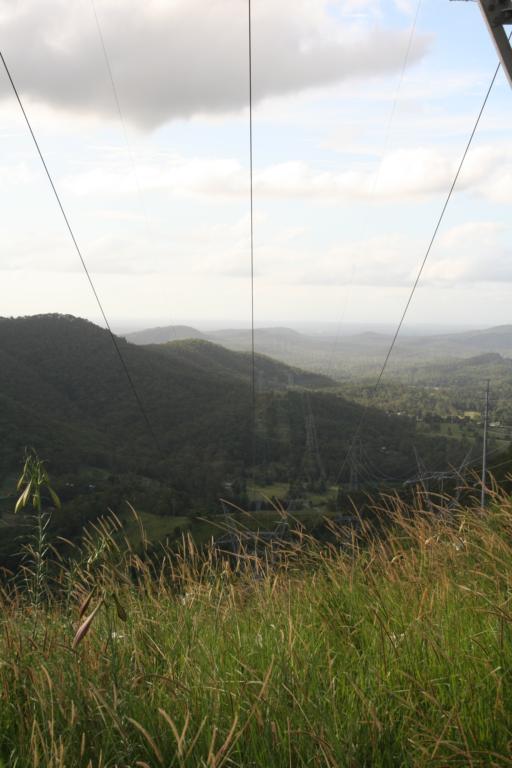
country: AU
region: Queensland
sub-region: Gold Coast
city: Upper Coomera
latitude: -27.8781
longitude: 153.2142
